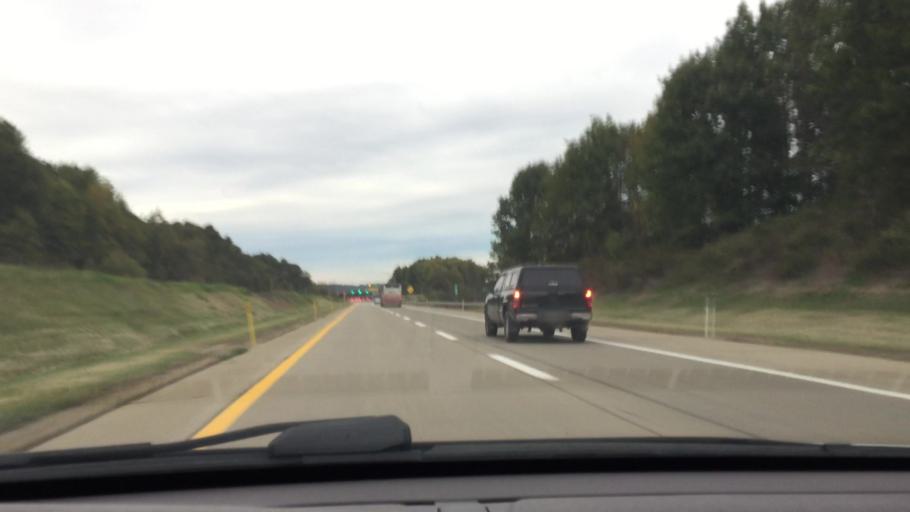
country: US
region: Pennsylvania
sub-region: Lawrence County
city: Oakland
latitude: 40.9383
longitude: -80.3914
